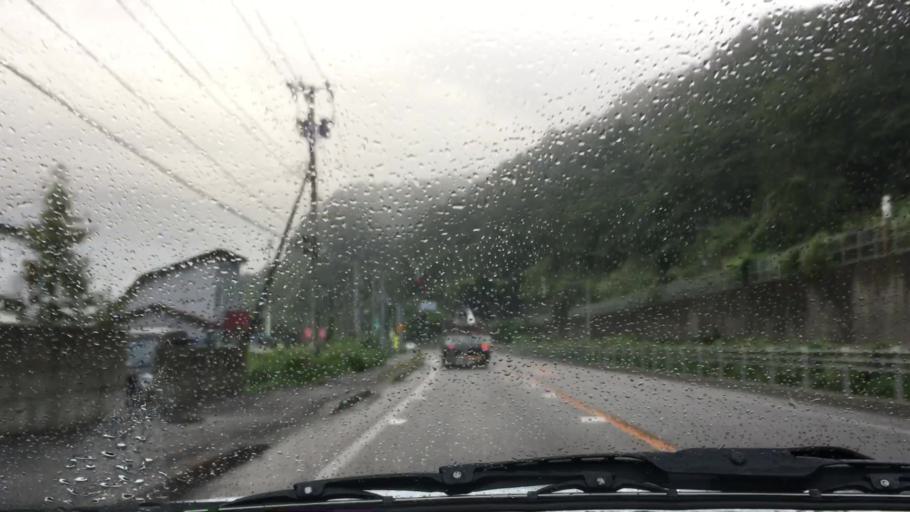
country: JP
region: Hokkaido
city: Nanae
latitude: 42.1578
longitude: 140.4748
